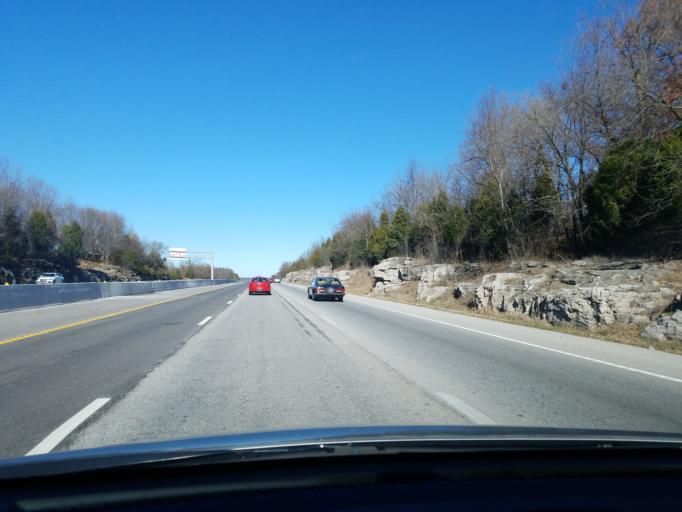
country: US
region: Missouri
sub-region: Christian County
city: Nixa
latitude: 37.1060
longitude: -93.2329
